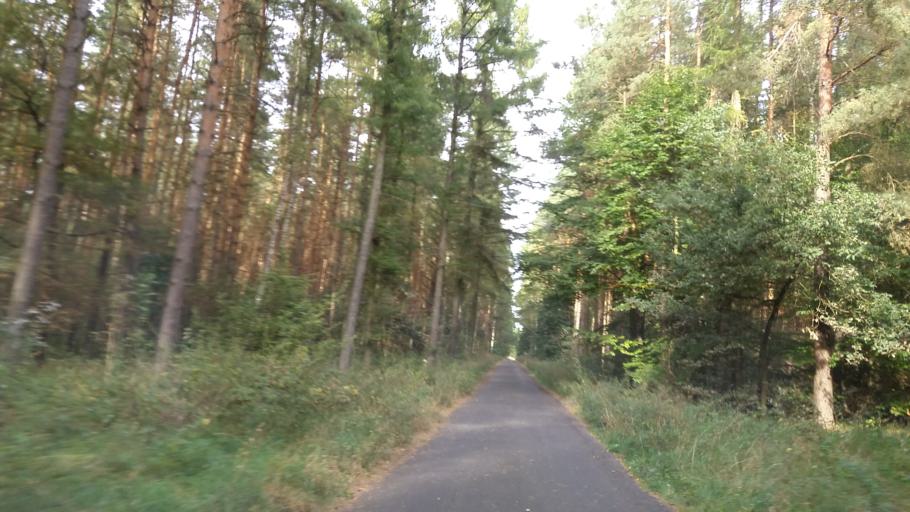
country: PL
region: West Pomeranian Voivodeship
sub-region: Powiat choszczenski
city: Krzecin
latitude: 52.9697
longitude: 15.4578
